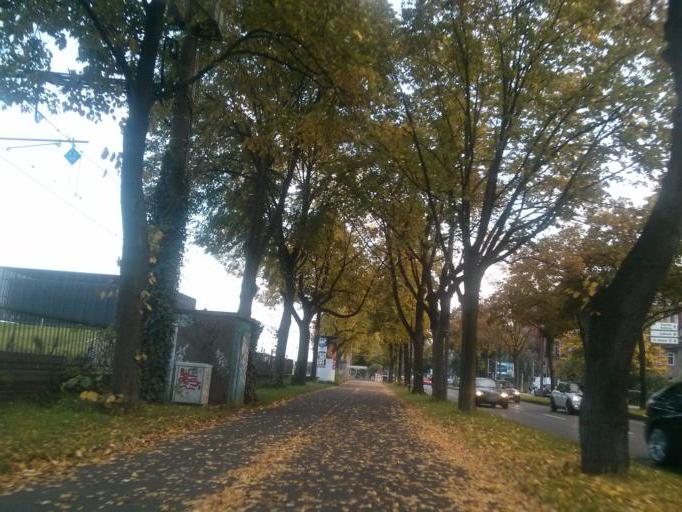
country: DE
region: North Rhine-Westphalia
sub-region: Regierungsbezirk Koln
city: Bayenthal
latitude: 50.9150
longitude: 6.9713
